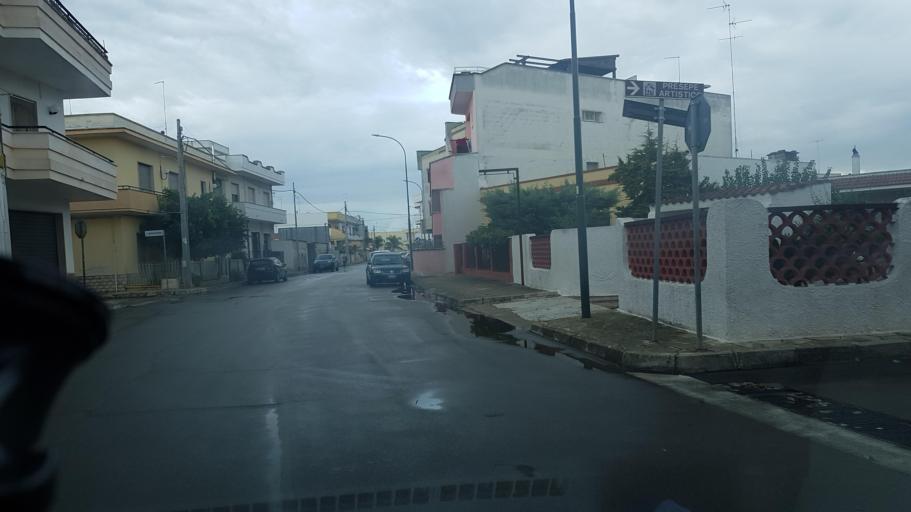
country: IT
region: Apulia
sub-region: Provincia di Lecce
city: Salice Salentino
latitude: 40.3885
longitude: 17.9596
